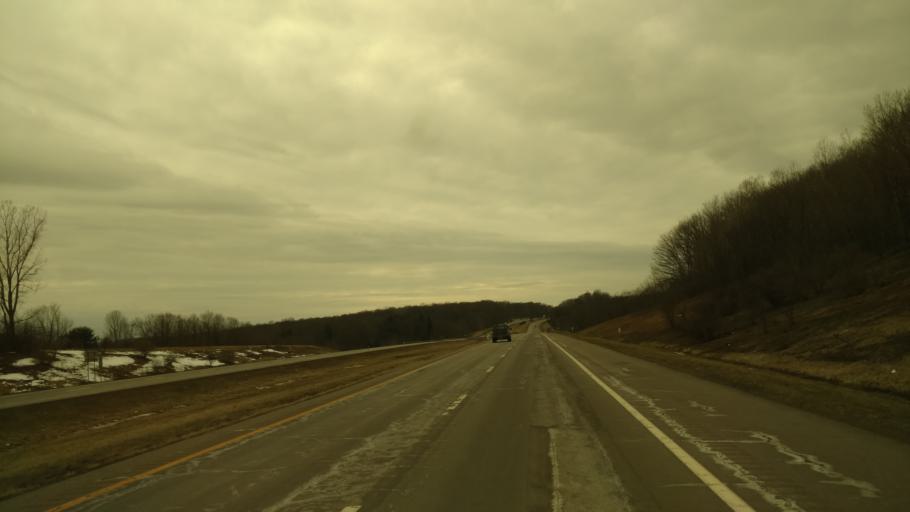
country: US
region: New York
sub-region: Chautauqua County
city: Celoron
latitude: 42.1284
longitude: -79.3050
